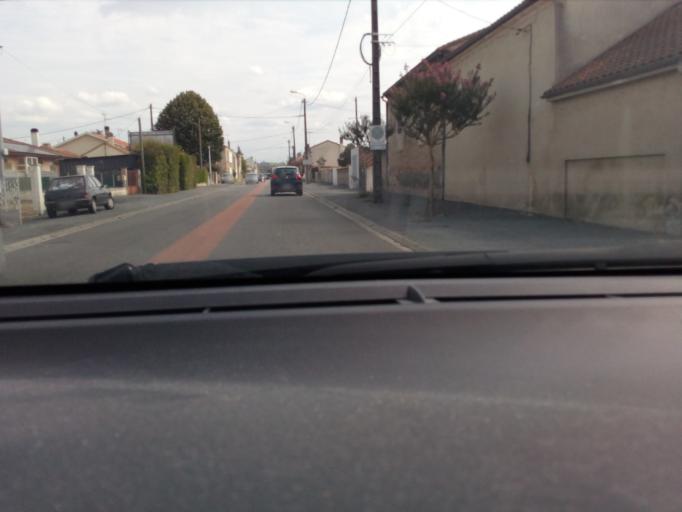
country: FR
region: Poitou-Charentes
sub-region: Departement de la Charente
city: Saint-Yrieix-sur-Charente
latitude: 45.6707
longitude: 0.1155
